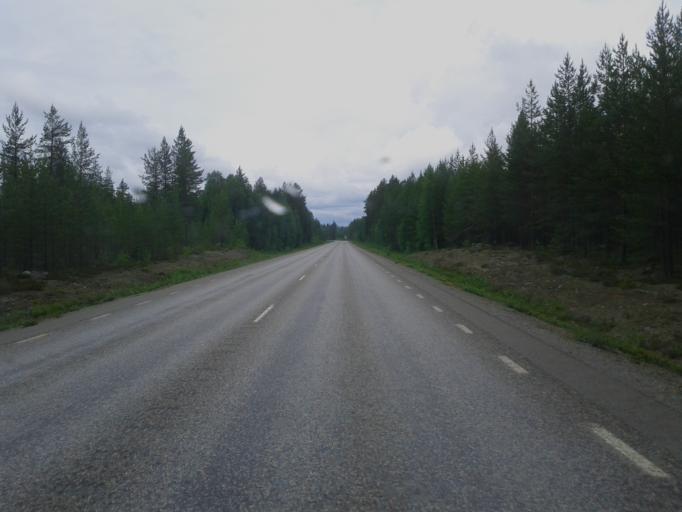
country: SE
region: Vaesterbotten
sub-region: Skelleftea Kommun
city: Langsele
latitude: 64.9549
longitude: 19.8999
